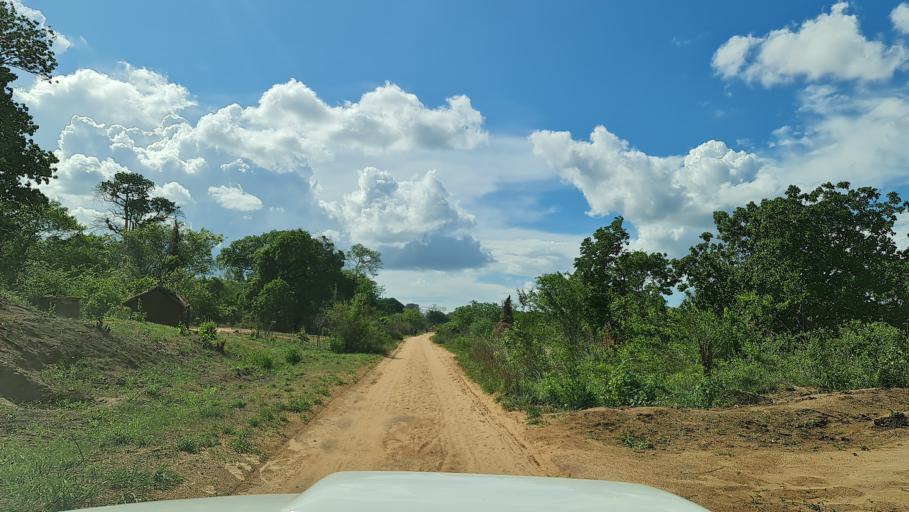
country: MZ
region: Nampula
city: Ilha de Mocambique
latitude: -15.4358
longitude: 40.2785
